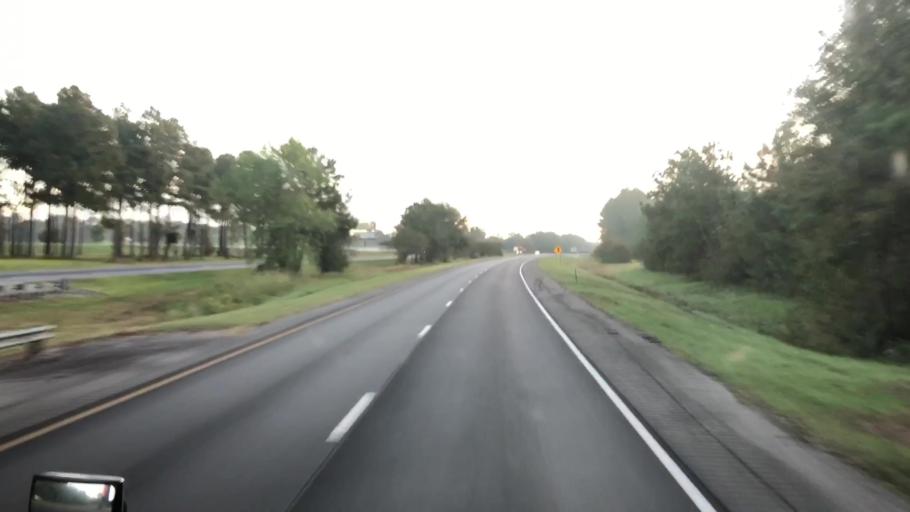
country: US
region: South Carolina
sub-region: Clarendon County
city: Manning
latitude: 33.5891
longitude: -80.3566
